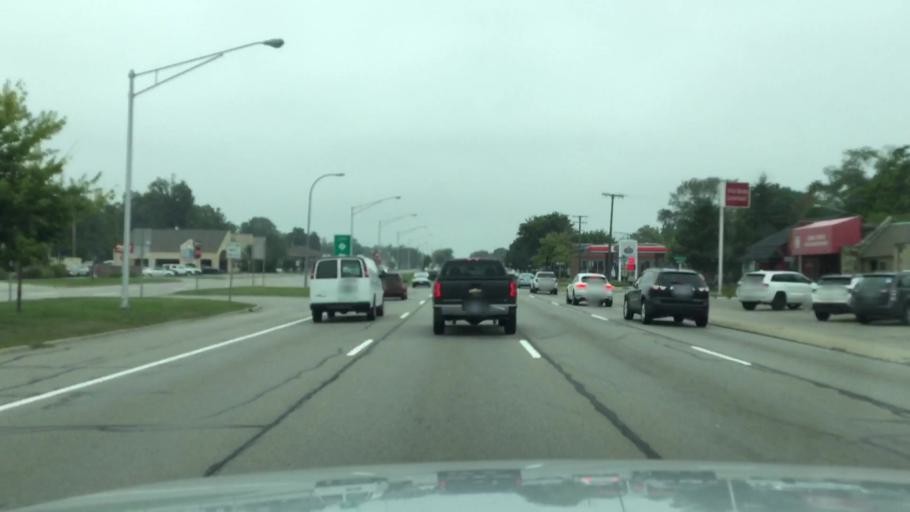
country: US
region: Michigan
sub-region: Oakland County
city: Berkley
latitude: 42.4989
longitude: -83.1677
